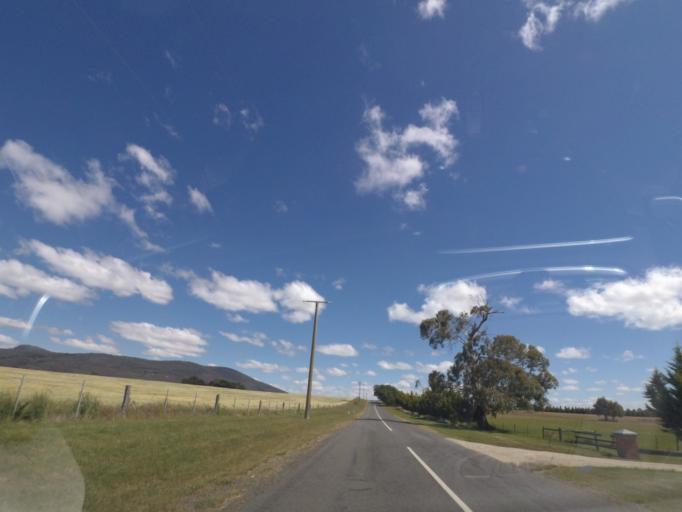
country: AU
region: Victoria
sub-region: Hume
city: Sunbury
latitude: -37.3322
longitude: 144.5587
